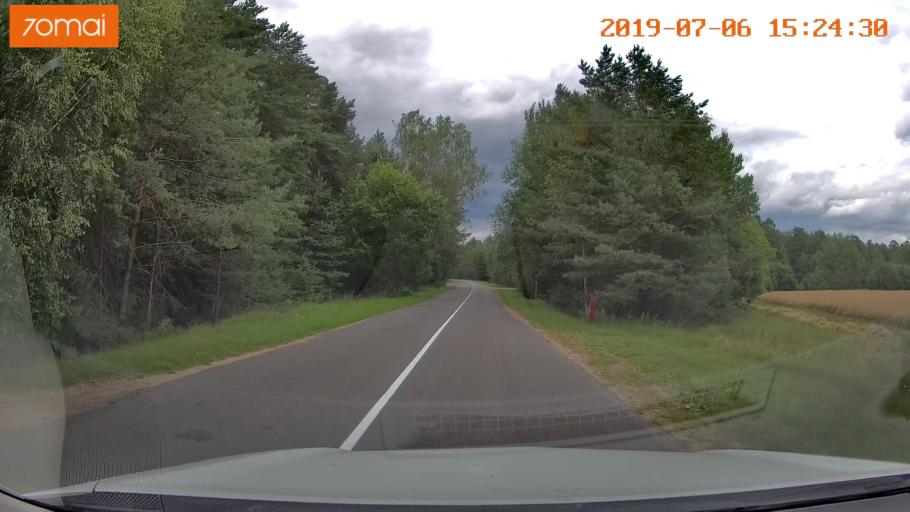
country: BY
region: Minsk
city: Valozhyn
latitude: 54.0203
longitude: 26.6027
